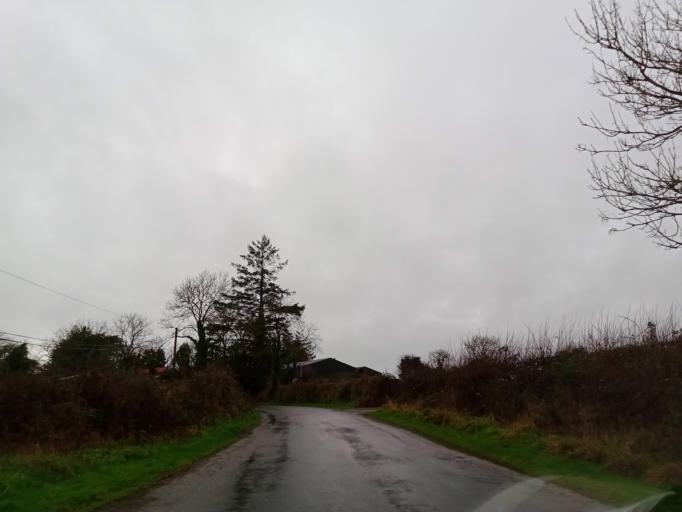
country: IE
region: Munster
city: Fethard
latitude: 52.5573
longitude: -7.6978
